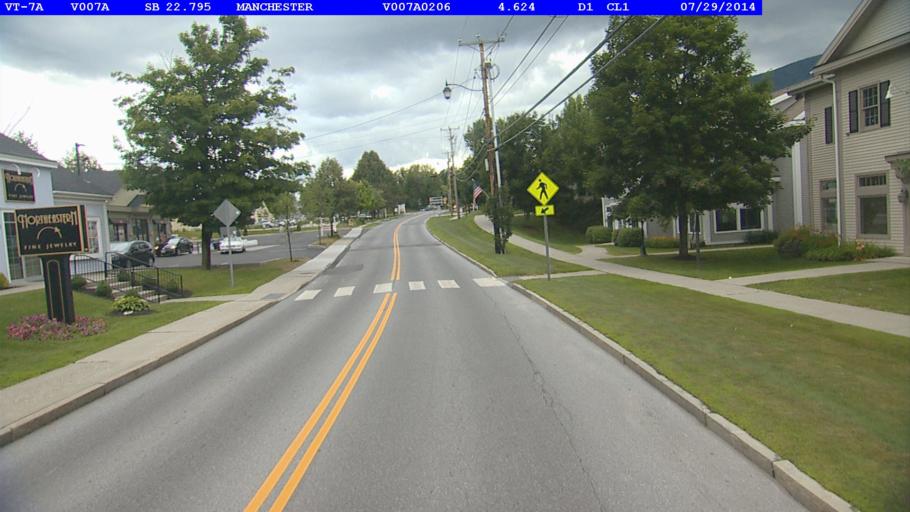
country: US
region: Vermont
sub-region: Bennington County
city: Manchester Center
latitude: 43.1743
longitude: -73.0603
